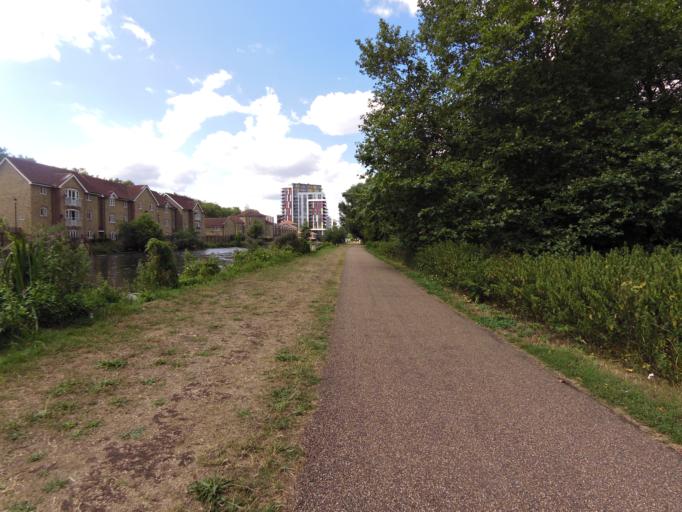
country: GB
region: England
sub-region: Greater London
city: Hackney
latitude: 51.5495
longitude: -0.0278
